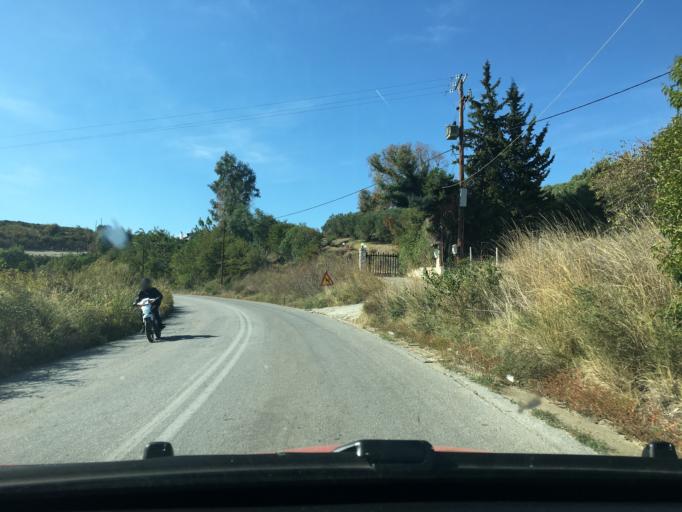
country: GR
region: Central Macedonia
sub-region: Nomos Chalkidikis
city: Nea Roda
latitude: 40.3805
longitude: 23.9145
